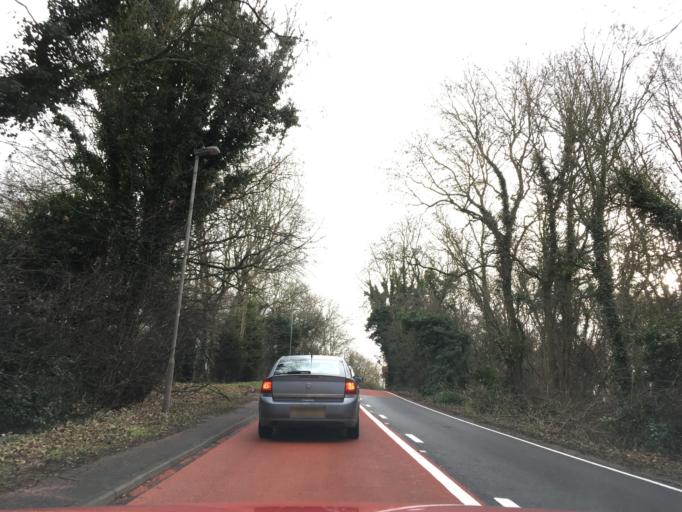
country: GB
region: England
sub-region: Nottinghamshire
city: Gotham
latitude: 52.8538
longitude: -1.1923
